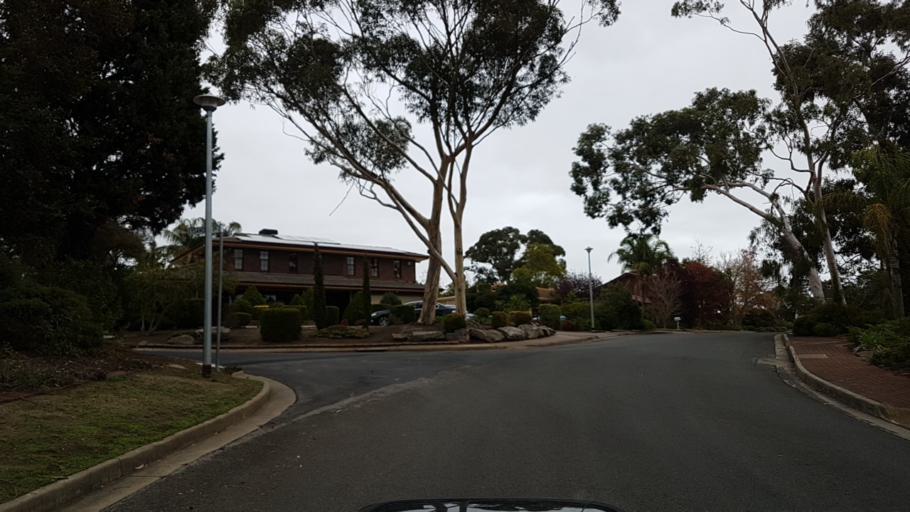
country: AU
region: South Australia
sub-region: Onkaparinga
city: Bedford Park
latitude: -35.0478
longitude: 138.5866
